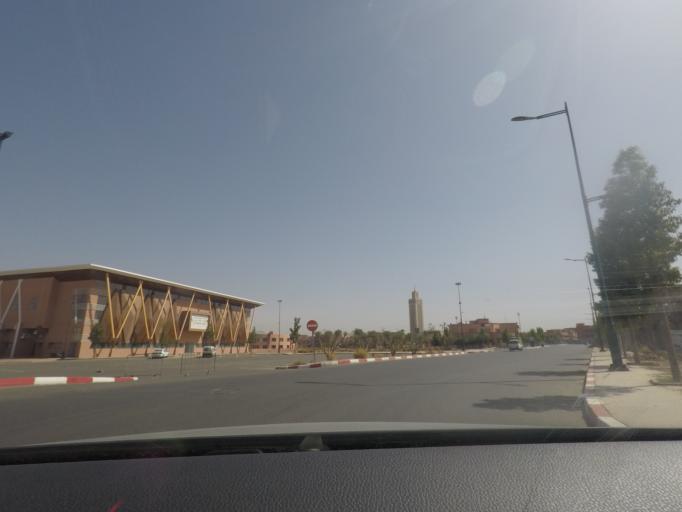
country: MA
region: Marrakech-Tensift-Al Haouz
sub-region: Marrakech
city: Marrakesh
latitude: 31.5900
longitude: -8.0293
